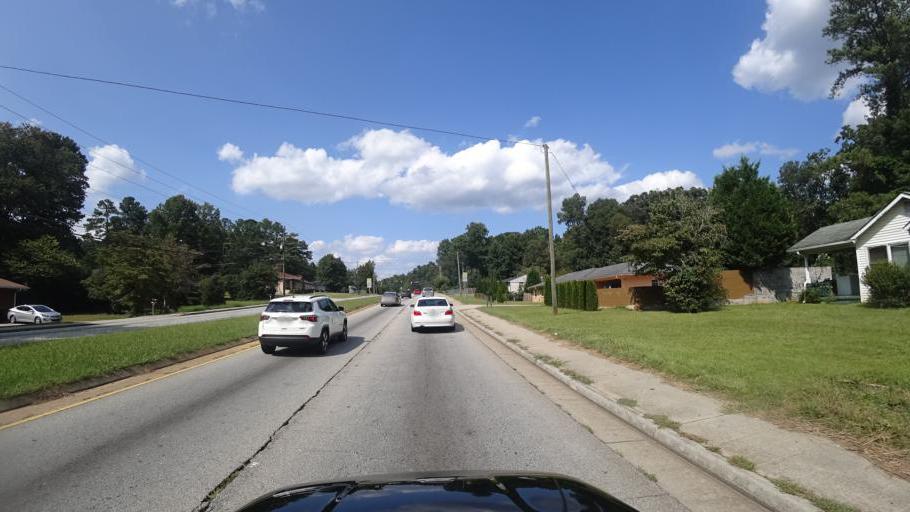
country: US
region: Georgia
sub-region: DeKalb County
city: Stone Mountain
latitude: 33.7921
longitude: -84.1946
